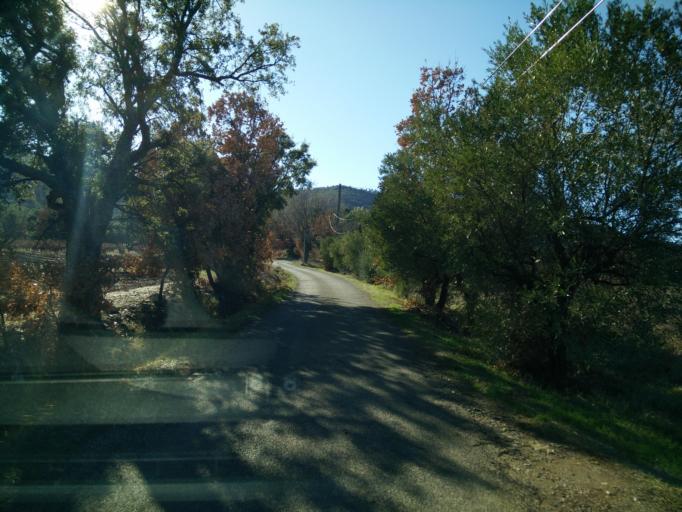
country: FR
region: Provence-Alpes-Cote d'Azur
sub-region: Departement du Var
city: Gonfaron
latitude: 43.3098
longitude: 6.2910
